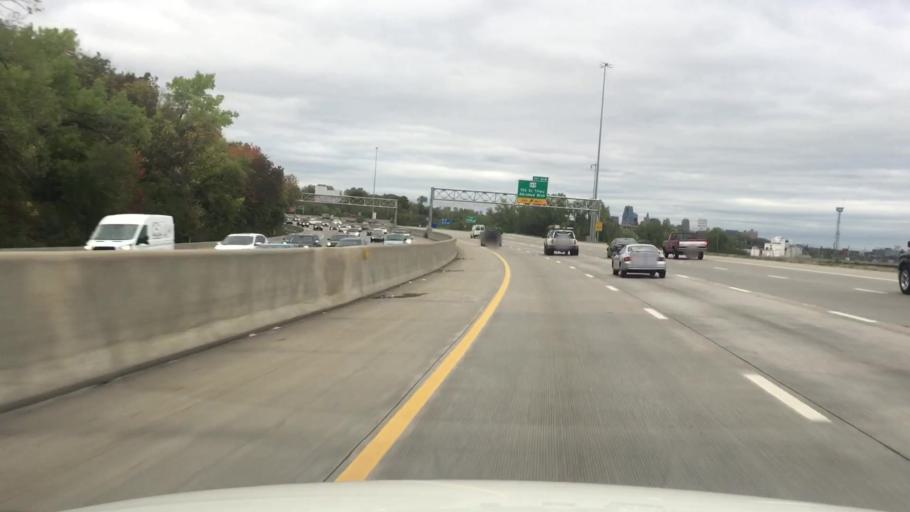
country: US
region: Kansas
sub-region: Johnson County
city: Westwood
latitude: 39.0664
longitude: -94.6212
